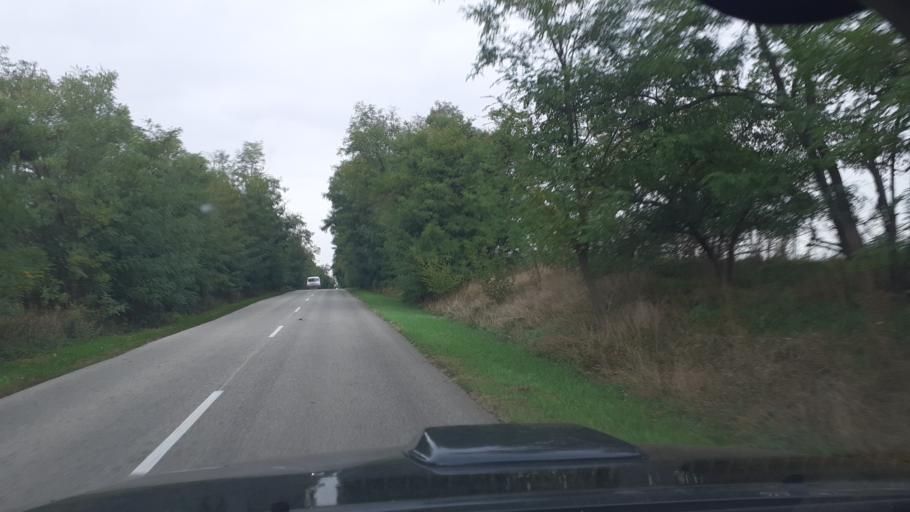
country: HU
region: Fejer
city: Baracs
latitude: 46.8472
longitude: 18.8869
